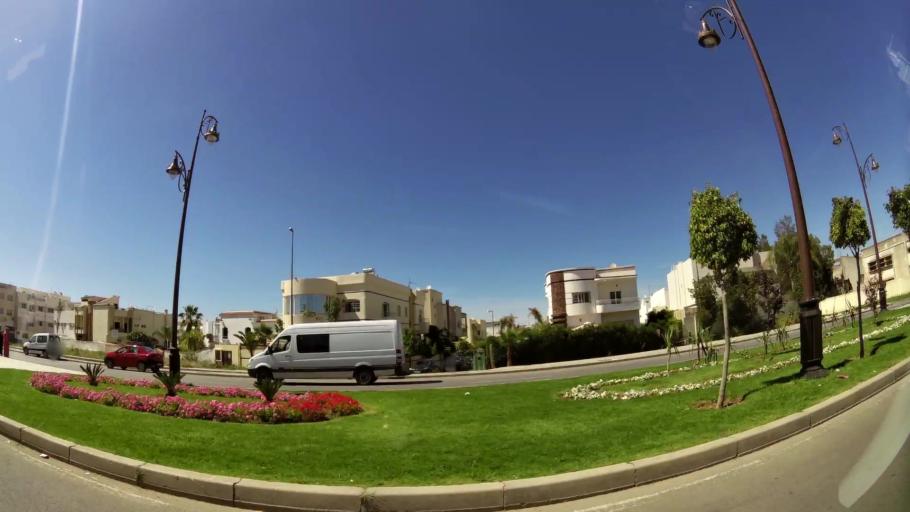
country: MA
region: Fes-Boulemane
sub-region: Fes
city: Fes
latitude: 34.0149
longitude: -4.9996
